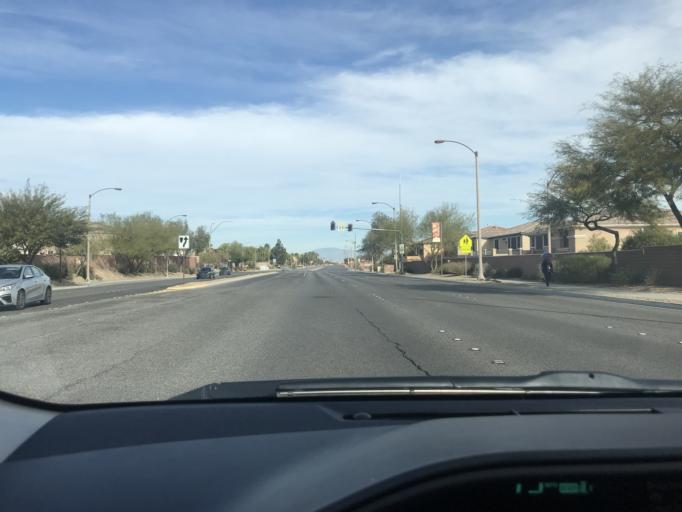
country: US
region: Nevada
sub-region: Clark County
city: Enterprise
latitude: 36.0109
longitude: -115.2799
